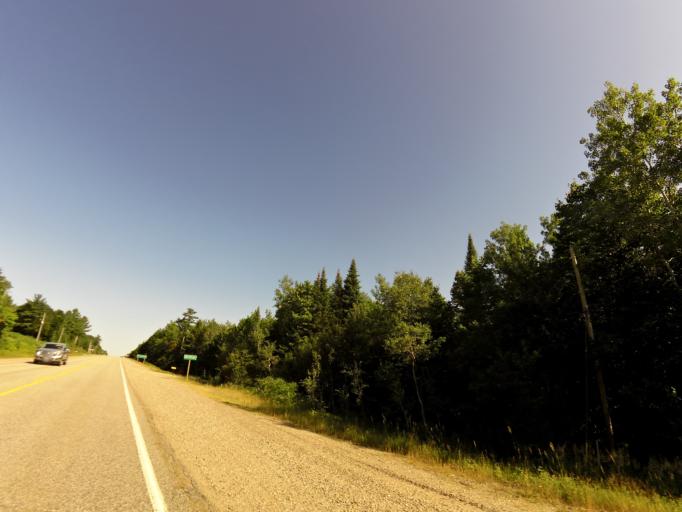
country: CA
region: Ontario
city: Deep River
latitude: 46.1575
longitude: -77.5953
